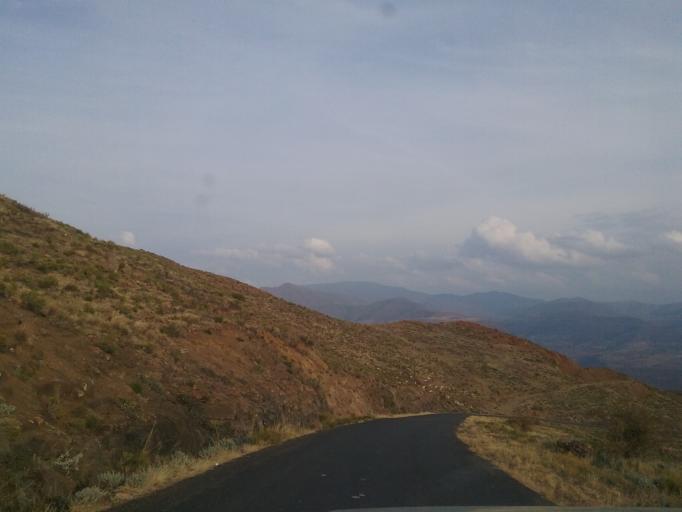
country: LS
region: Quthing
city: Quthing
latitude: -30.1965
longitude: 27.9708
